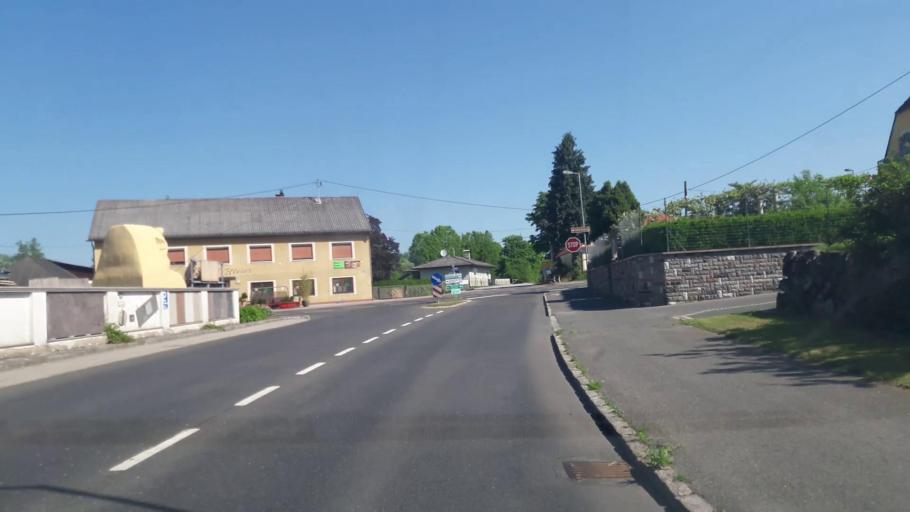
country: AT
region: Styria
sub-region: Politischer Bezirk Hartberg-Fuerstenfeld
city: Burgau
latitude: 47.1520
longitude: 16.1141
